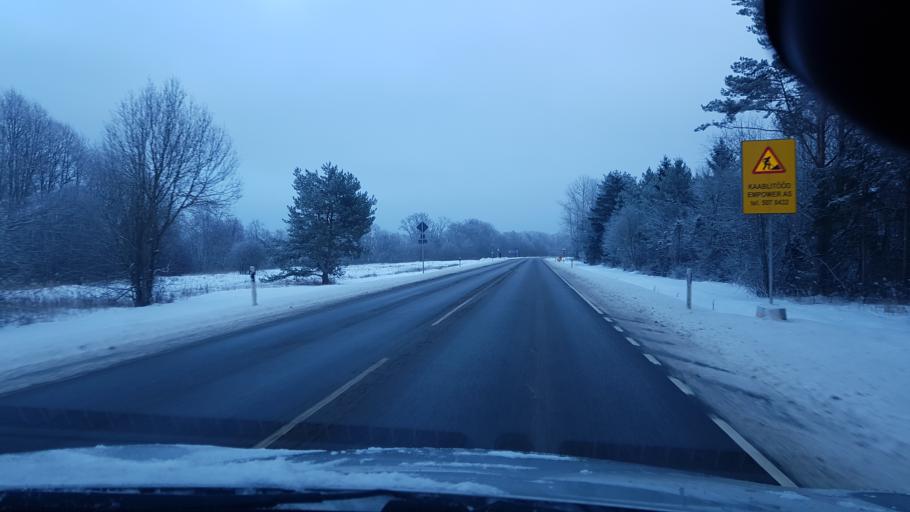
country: EE
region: Harju
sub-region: Paldiski linn
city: Paldiski
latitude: 59.3438
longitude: 24.1905
